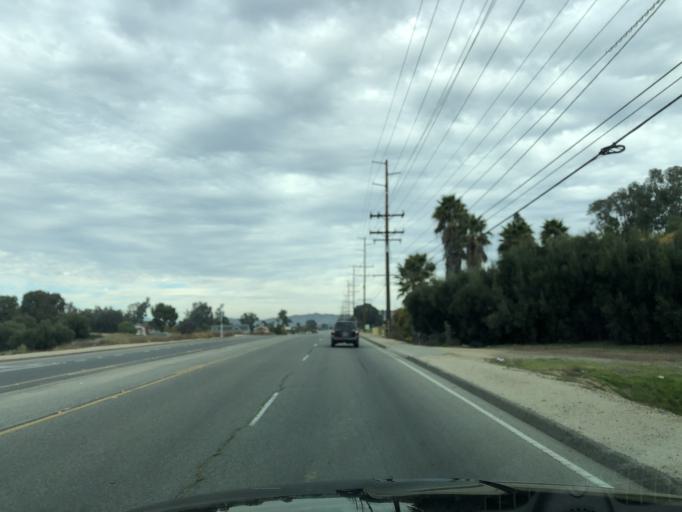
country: US
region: California
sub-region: Riverside County
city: Wildomar
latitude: 33.6150
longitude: -117.2896
